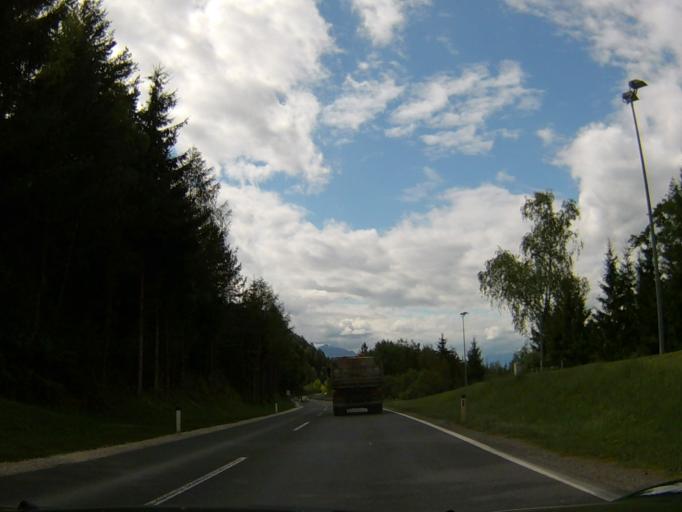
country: AT
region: Carinthia
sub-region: Politischer Bezirk Villach Land
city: Fresach
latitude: 46.6659
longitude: 13.7287
